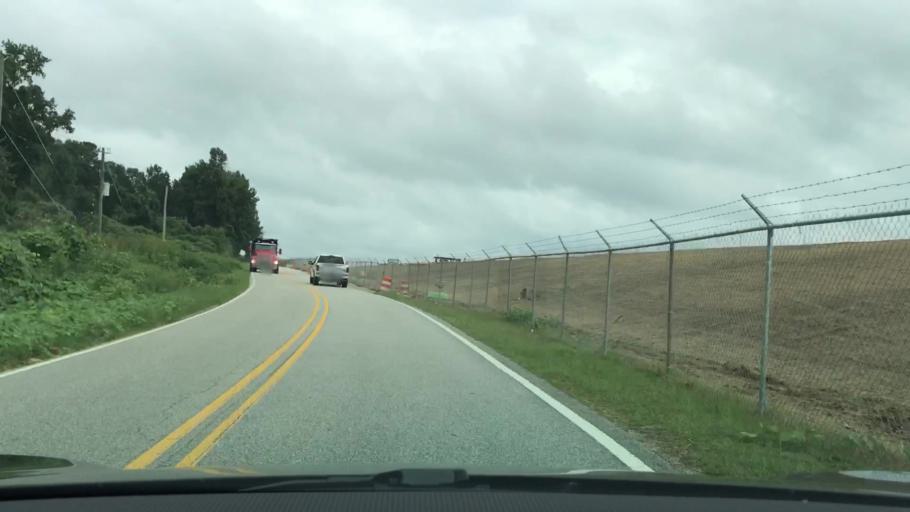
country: US
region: Alabama
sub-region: Lee County
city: Auburn
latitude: 32.6157
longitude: -85.4383
